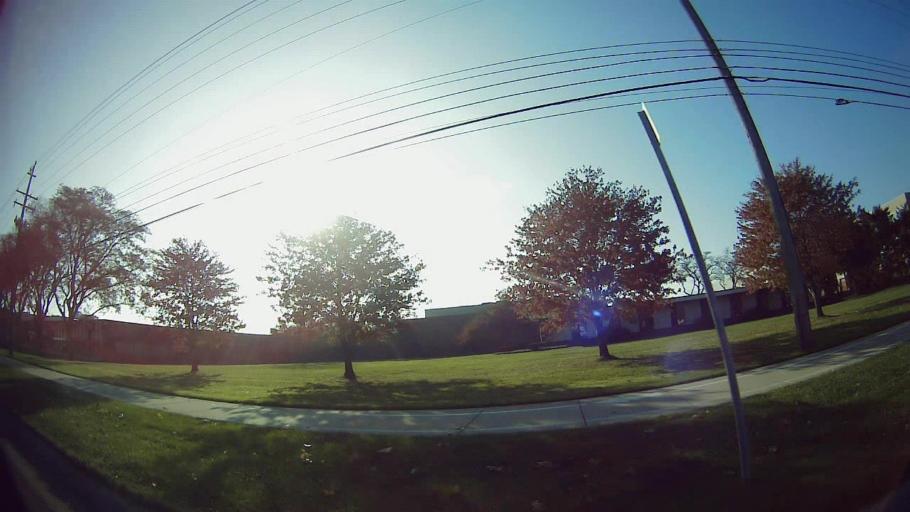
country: US
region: Michigan
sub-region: Oakland County
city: Clawson
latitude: 42.5476
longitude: -83.1772
